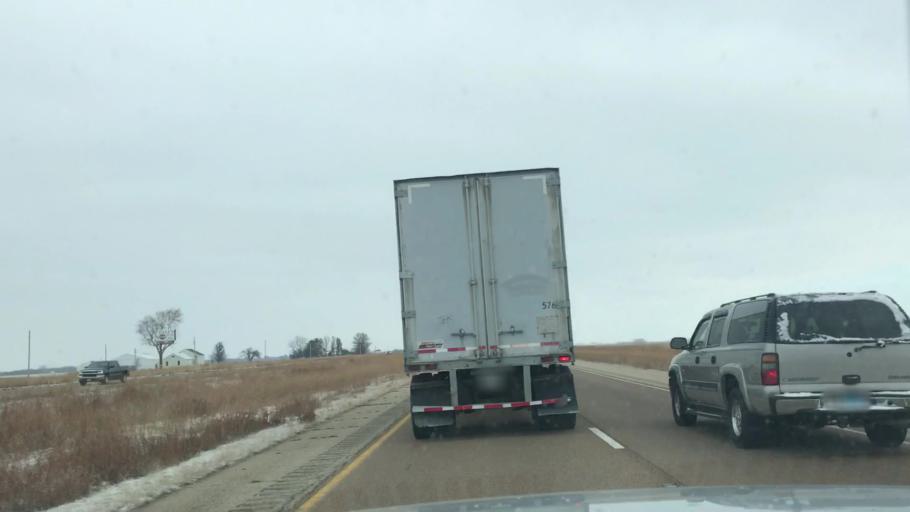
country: US
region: Illinois
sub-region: Montgomery County
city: Raymond
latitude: 39.3969
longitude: -89.6431
